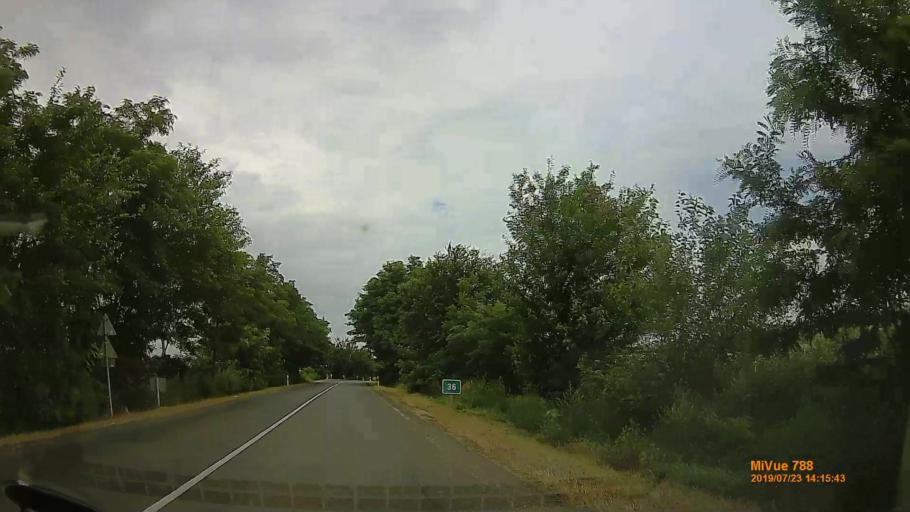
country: HU
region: Szabolcs-Szatmar-Bereg
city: Nagycserkesz
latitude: 47.9598
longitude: 21.5189
